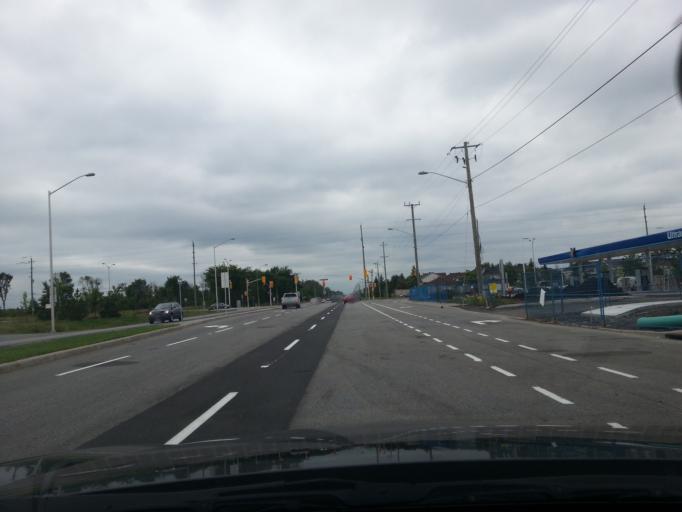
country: CA
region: Ontario
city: Ottawa
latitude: 45.3747
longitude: -75.5958
